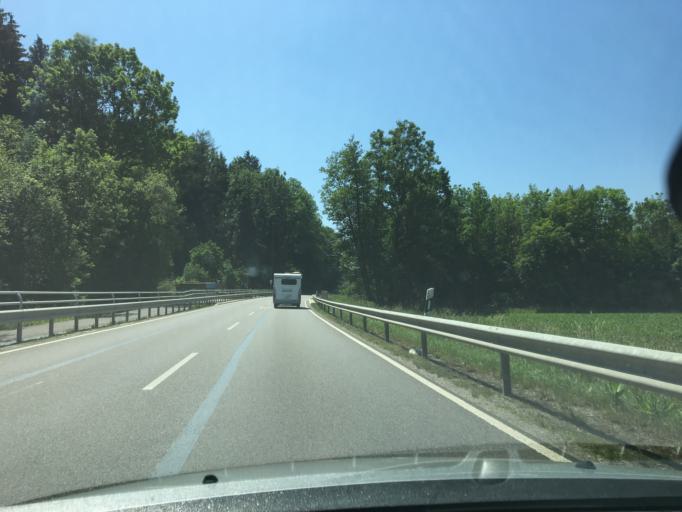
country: DE
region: Bavaria
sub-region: Upper Bavaria
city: Rohrbach
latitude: 48.2923
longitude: 12.5607
